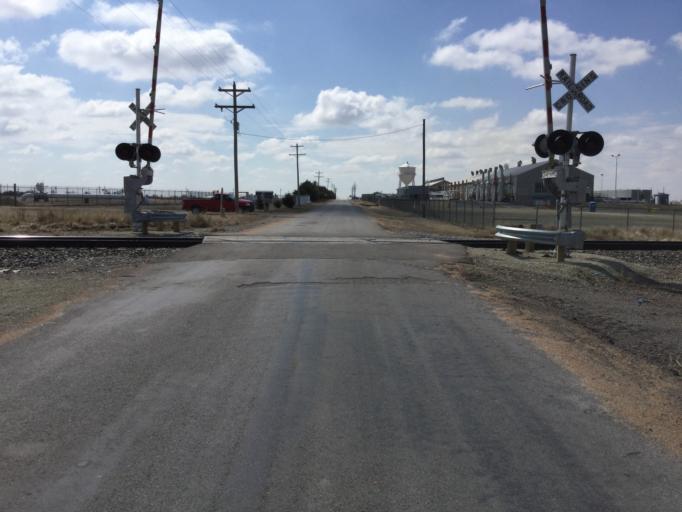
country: US
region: Kansas
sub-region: Kiowa County
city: Greensburg
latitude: 37.5929
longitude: -99.4124
